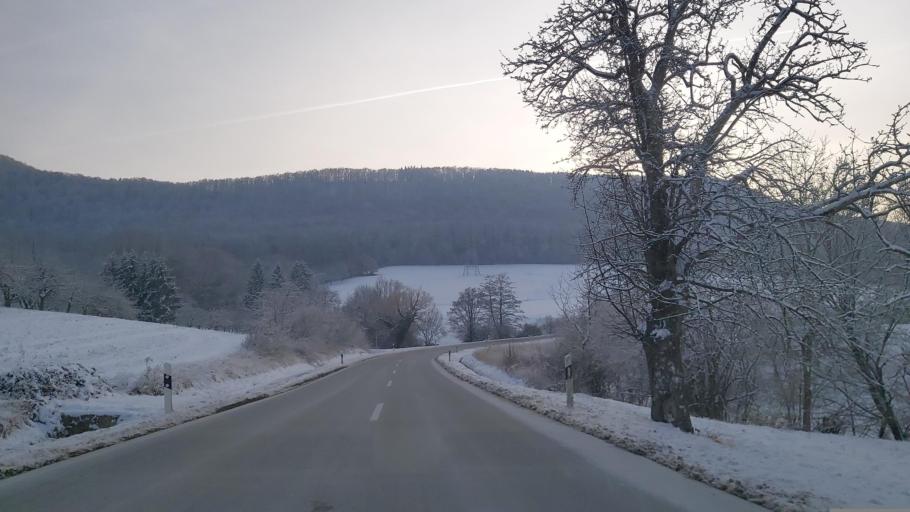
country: DE
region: Baden-Wuerttemberg
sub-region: Tuebingen Region
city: Metzingen
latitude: 48.5042
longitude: 9.2897
